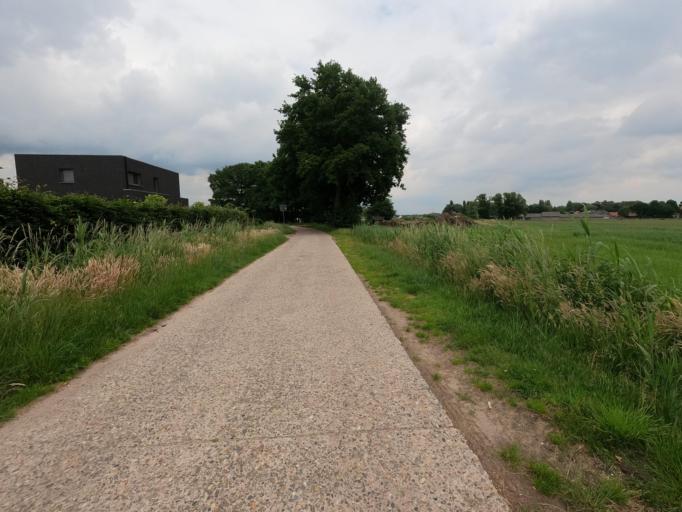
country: BE
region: Flanders
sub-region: Provincie Antwerpen
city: Kalmthout
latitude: 51.3730
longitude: 4.4944
